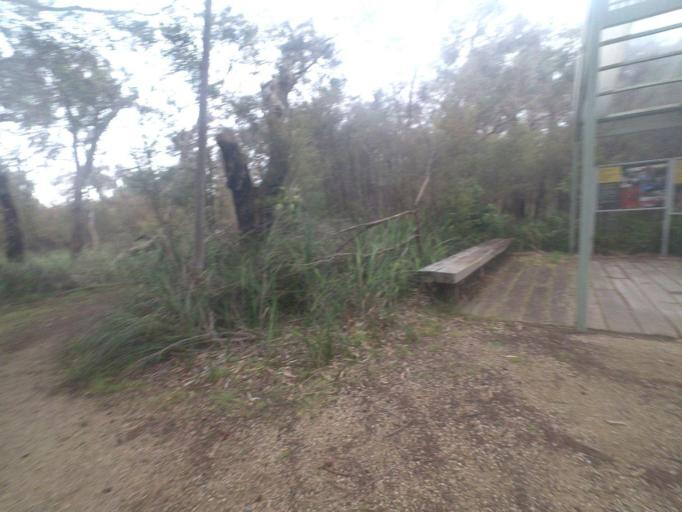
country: AU
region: Victoria
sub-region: Casey
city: Junction Village
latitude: -38.1372
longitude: 145.2835
